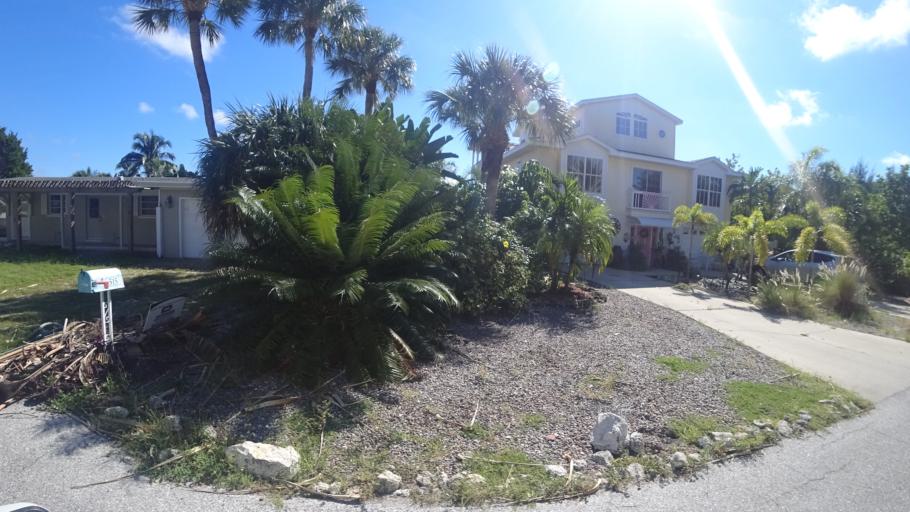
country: US
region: Florida
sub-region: Manatee County
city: Holmes Beach
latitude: 27.5112
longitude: -82.7120
